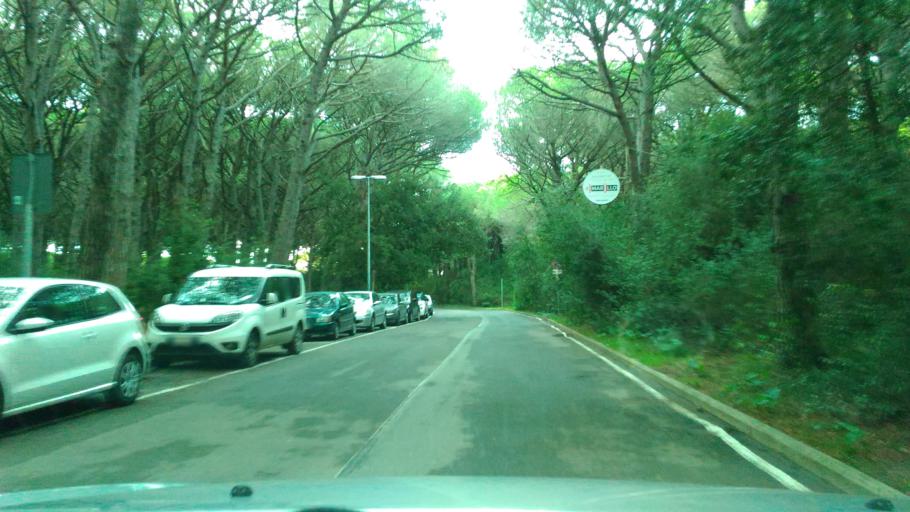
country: IT
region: Tuscany
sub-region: Provincia di Livorno
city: Cecina
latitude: 43.2932
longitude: 10.5046
